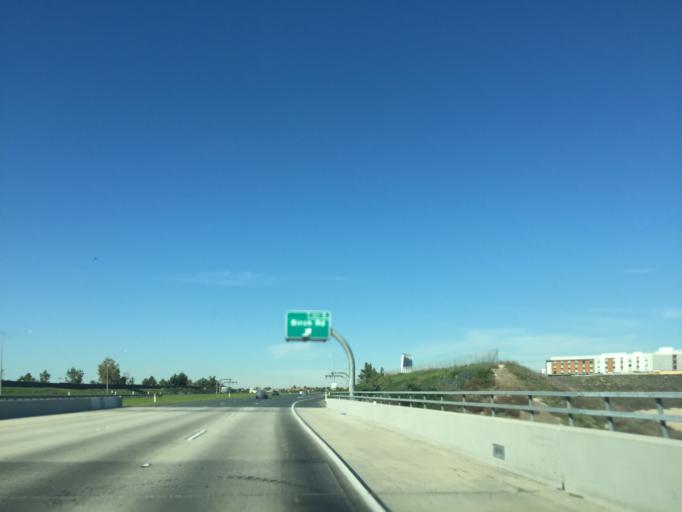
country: US
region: California
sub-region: San Diego County
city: Bonita
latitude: 32.6146
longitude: -116.9706
